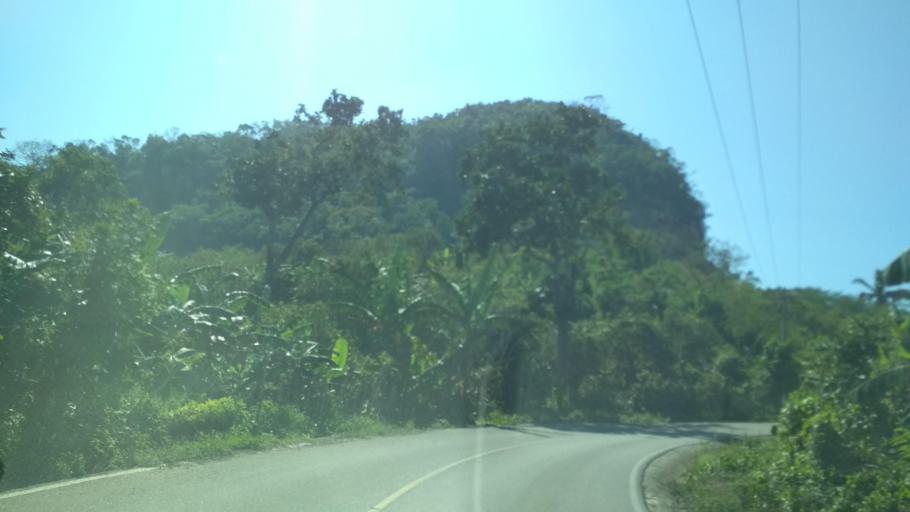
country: MX
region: Veracruz
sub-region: Papantla
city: Polutla
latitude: 20.4743
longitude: -97.2136
